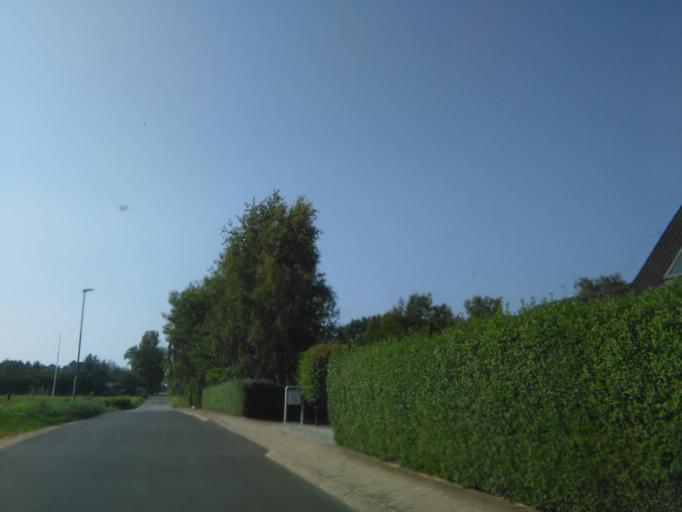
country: DK
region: Central Jutland
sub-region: Syddjurs Kommune
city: Ronde
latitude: 56.1952
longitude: 10.4323
